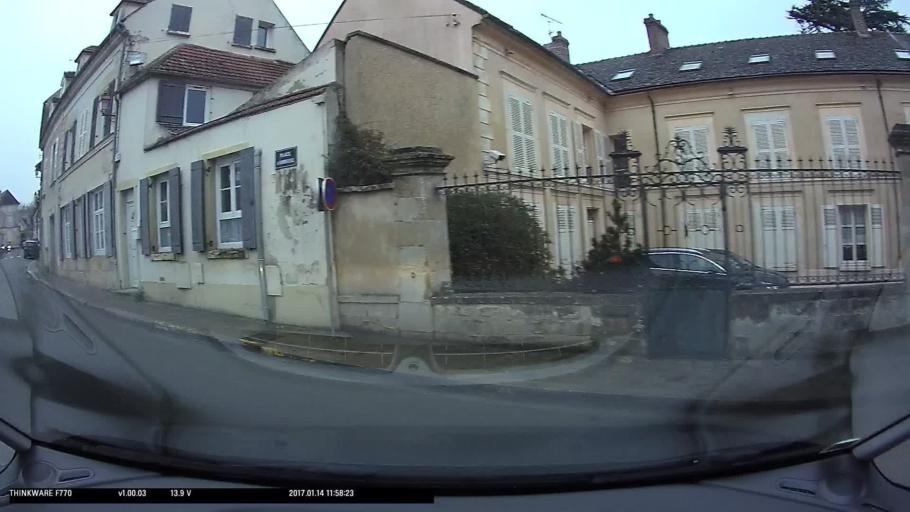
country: FR
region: Ile-de-France
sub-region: Departement du Val-d'Oise
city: Vigny
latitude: 49.0769
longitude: 1.9273
